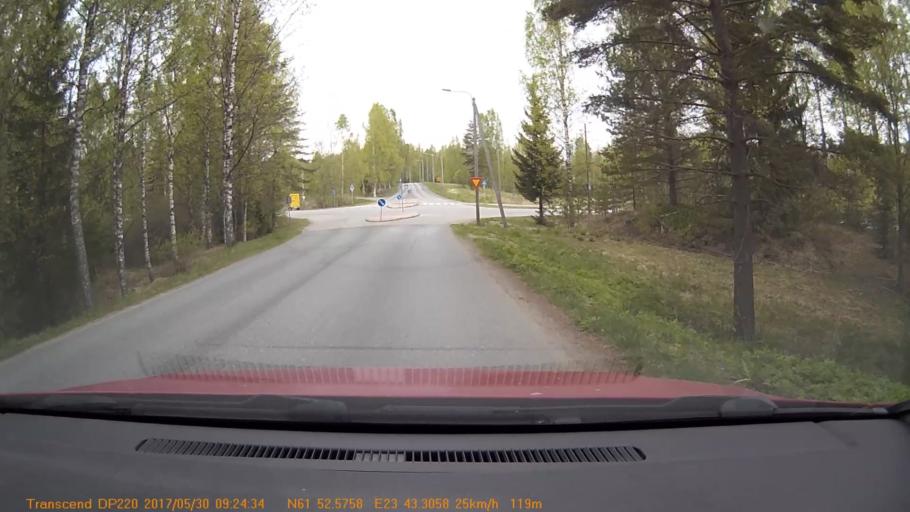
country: FI
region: Pirkanmaa
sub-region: Tampere
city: Kuru
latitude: 61.8762
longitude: 23.7218
